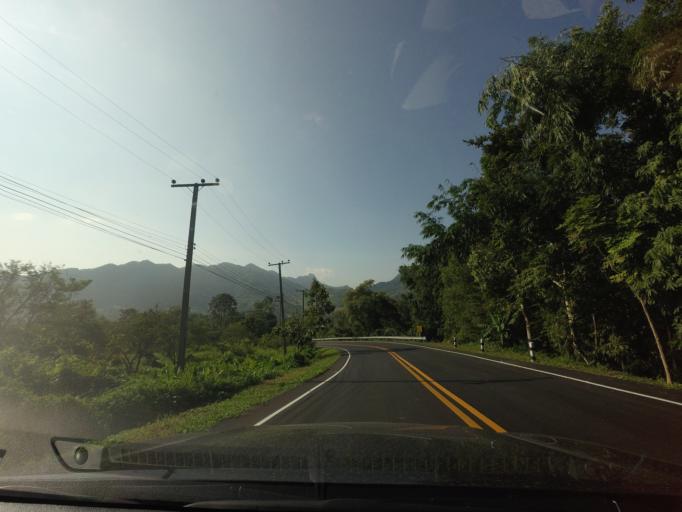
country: TH
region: Phetchabun
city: Lom Kao
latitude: 16.8712
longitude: 101.1328
